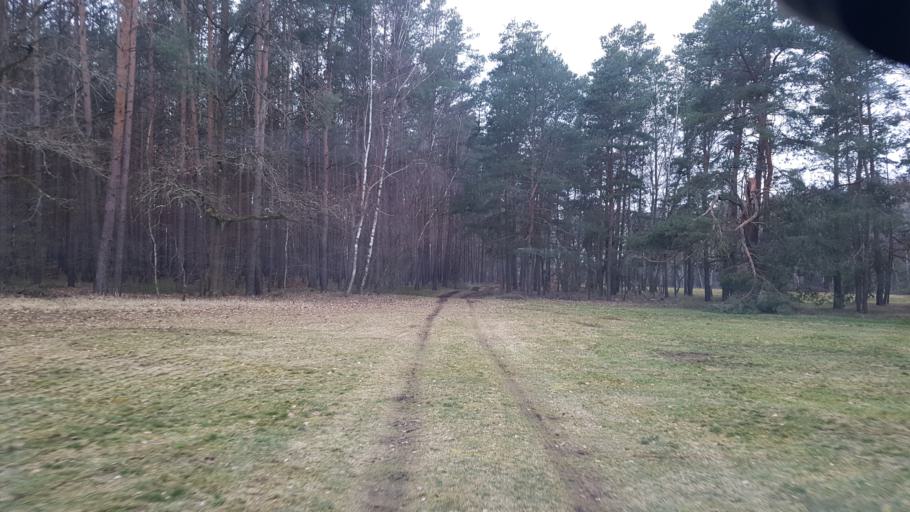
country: DE
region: Brandenburg
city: Schonborn
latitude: 51.6033
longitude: 13.5077
